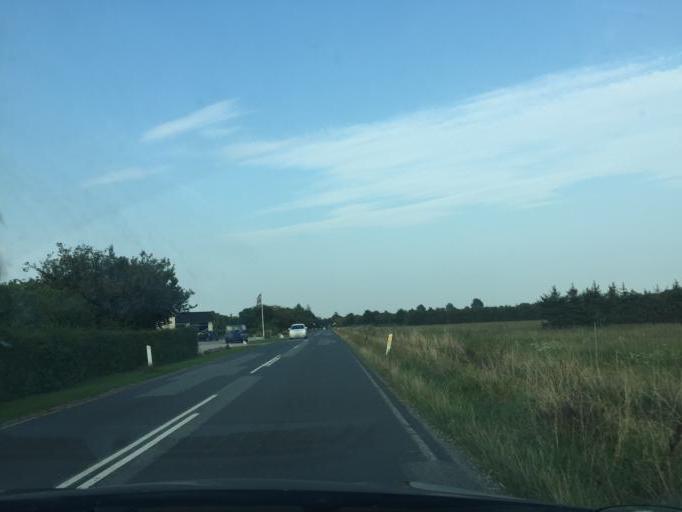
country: DK
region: South Denmark
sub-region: Kerteminde Kommune
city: Langeskov
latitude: 55.2894
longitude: 10.5581
